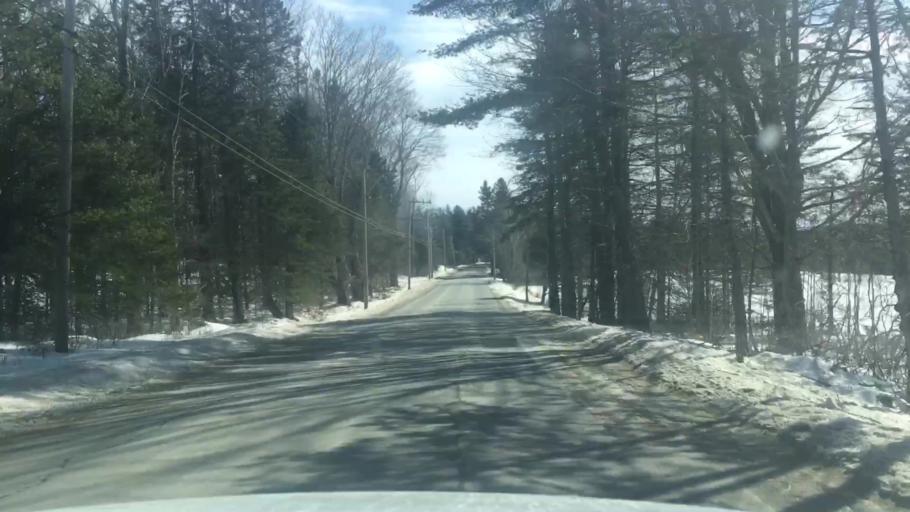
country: US
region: Maine
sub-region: Penobscot County
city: Holden
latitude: 44.7555
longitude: -68.6366
